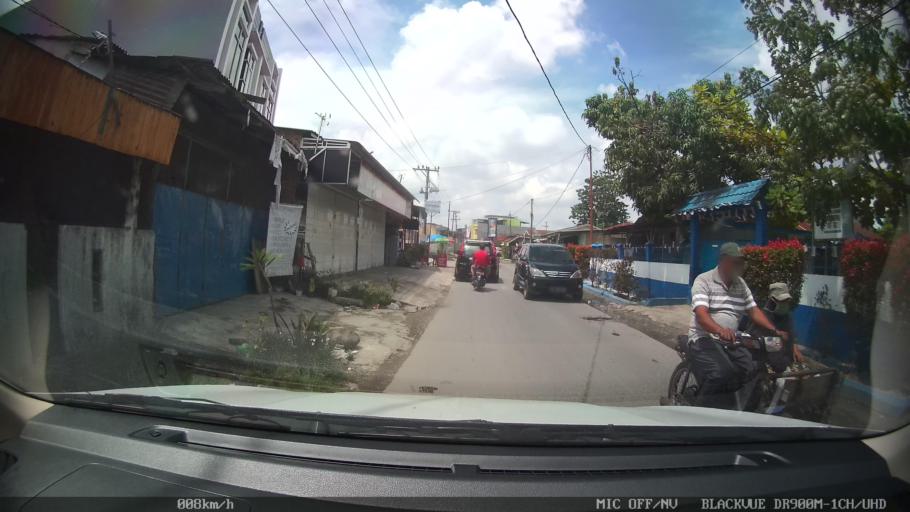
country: ID
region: North Sumatra
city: Medan
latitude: 3.6083
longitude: 98.7585
